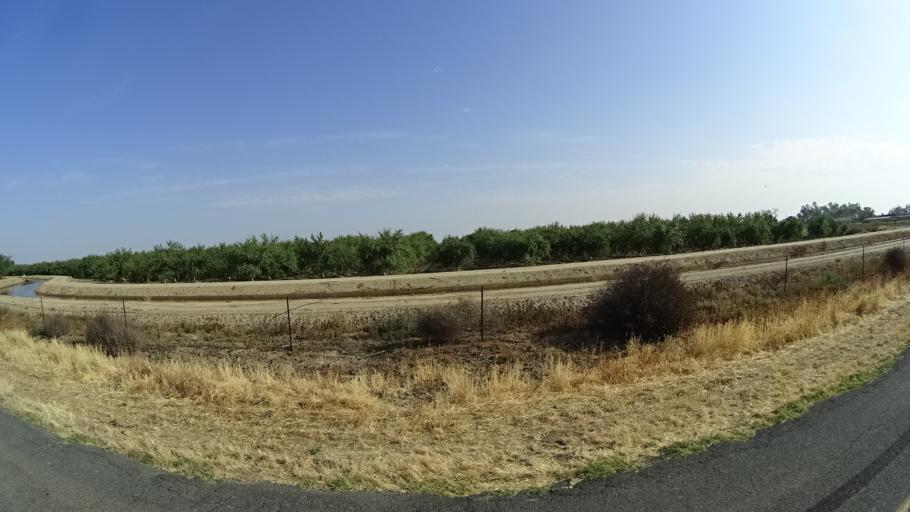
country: US
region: California
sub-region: Fresno County
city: Riverdale
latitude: 36.3584
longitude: -119.8459
